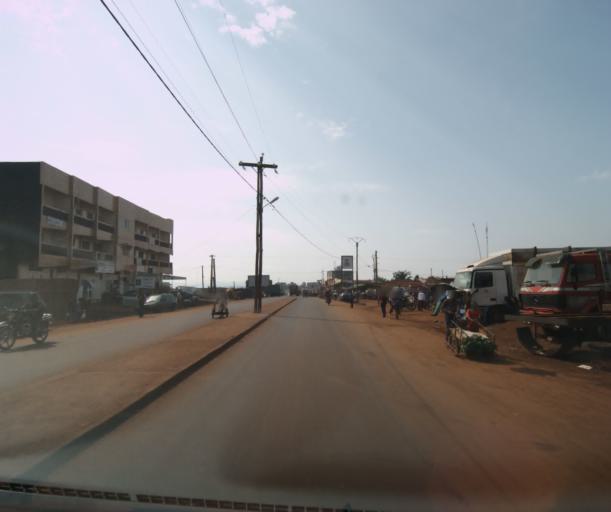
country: CM
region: West
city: Mbouda
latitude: 5.6241
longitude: 10.2636
